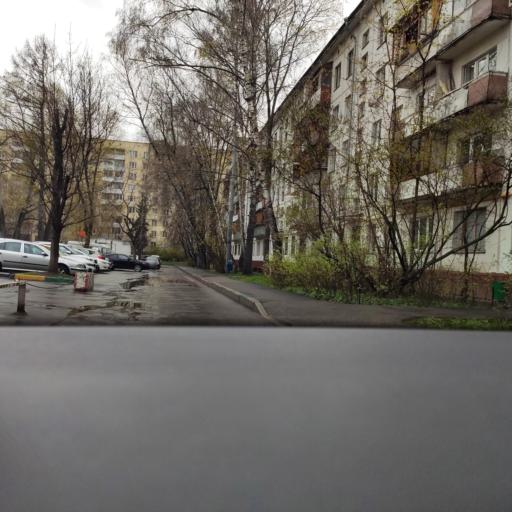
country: RU
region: Moscow
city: Gol'yanovo
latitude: 55.8152
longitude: 37.8190
